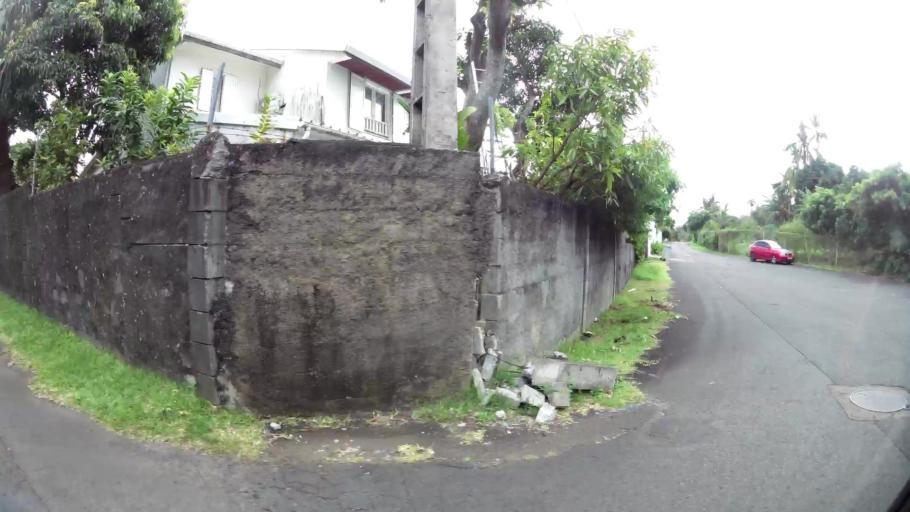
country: RE
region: Reunion
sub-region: Reunion
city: Sainte-Suzanne
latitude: -20.9004
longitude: 55.6000
